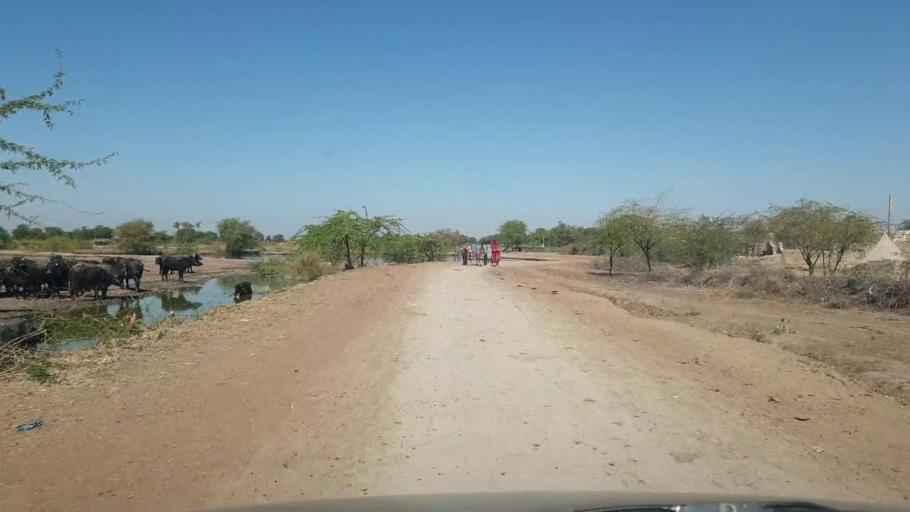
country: PK
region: Sindh
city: Umarkot
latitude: 25.4211
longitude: 69.6445
